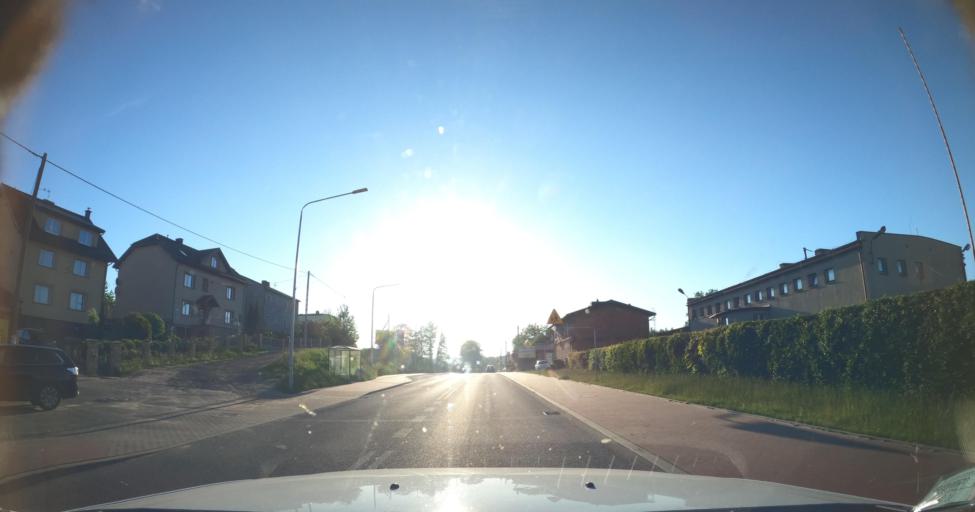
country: PL
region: Pomeranian Voivodeship
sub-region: Powiat kartuski
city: Chmielno
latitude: 54.3402
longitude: 18.0196
